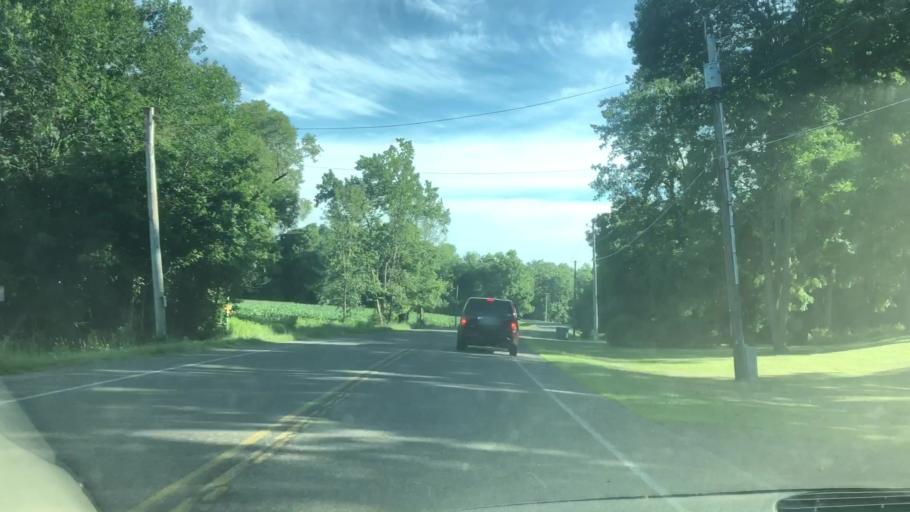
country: US
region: New York
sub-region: Wayne County
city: Macedon
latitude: 43.0465
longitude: -77.3389
